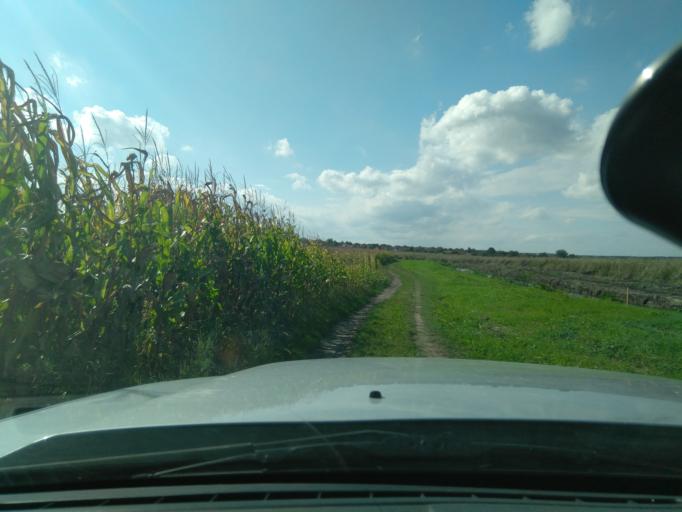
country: HU
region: Fejer
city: Bicske
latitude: 47.4819
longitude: 18.6630
